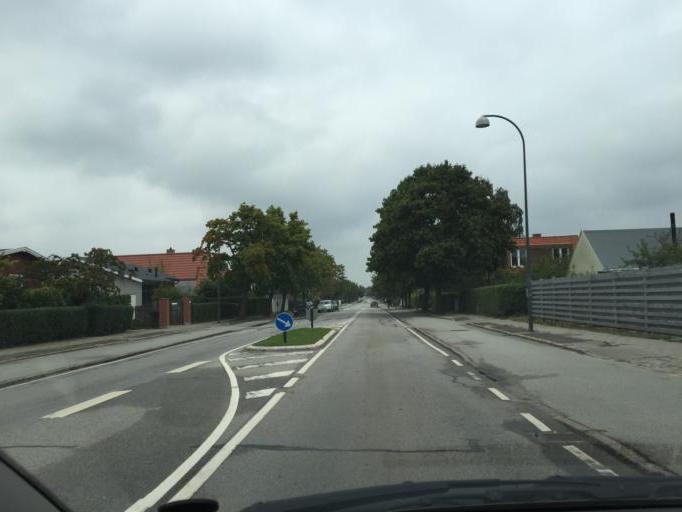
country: DK
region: Capital Region
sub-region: Herlev Kommune
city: Herlev
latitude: 55.7297
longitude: 12.4369
